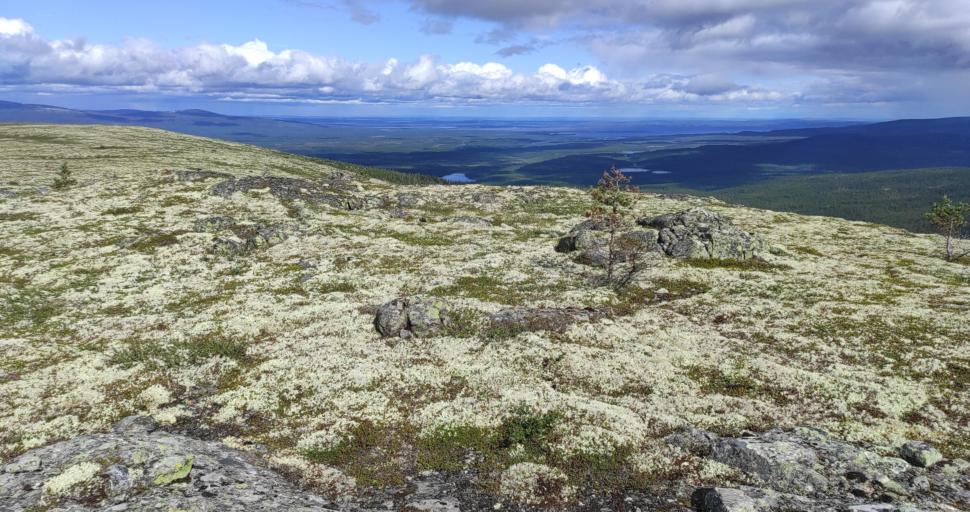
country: RU
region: Murmansk
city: Afrikanda
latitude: 67.0447
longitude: 32.9520
